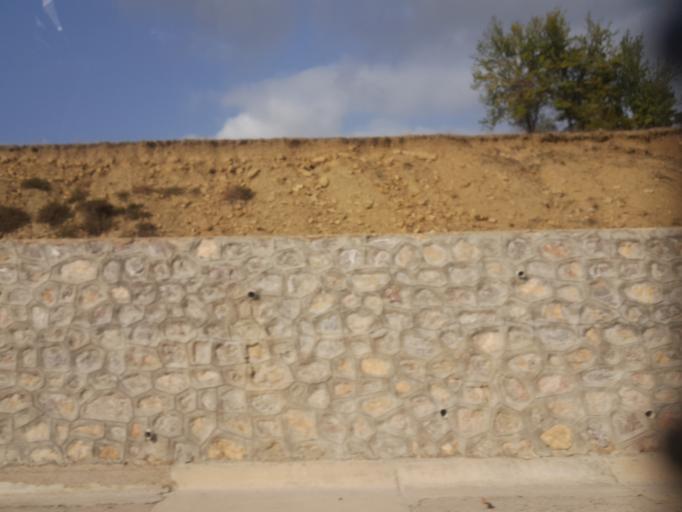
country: TR
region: Sinop
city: Duragan
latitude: 41.4974
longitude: 35.0361
